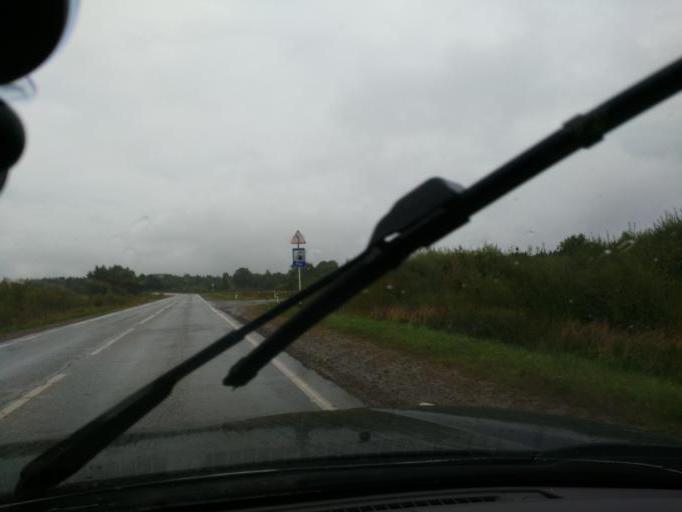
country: RU
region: Perm
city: Osa
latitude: 57.3943
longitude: 55.6151
